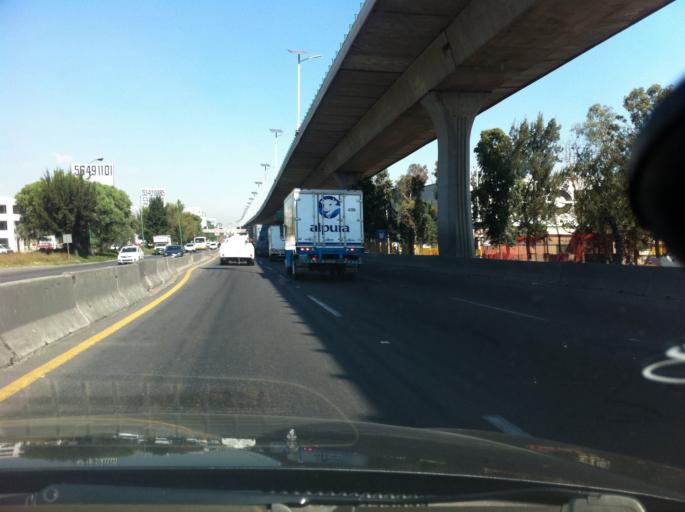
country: MX
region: Mexico
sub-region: Tultitlan
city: Buenavista
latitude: 19.6084
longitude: -99.1898
